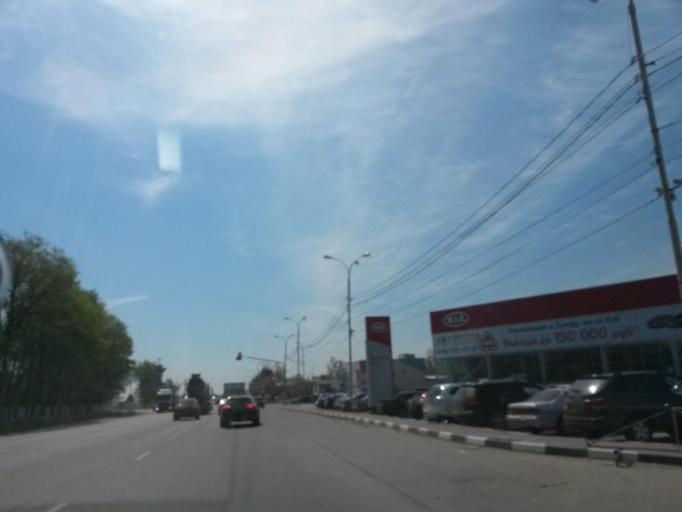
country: RU
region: Moskovskaya
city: Shcherbinka
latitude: 55.4680
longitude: 37.5612
